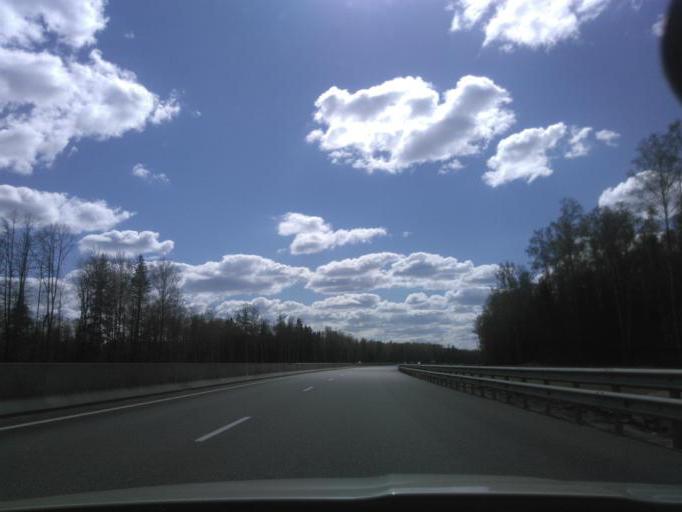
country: RU
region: Moskovskaya
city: Peshki
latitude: 56.1364
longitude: 37.1008
